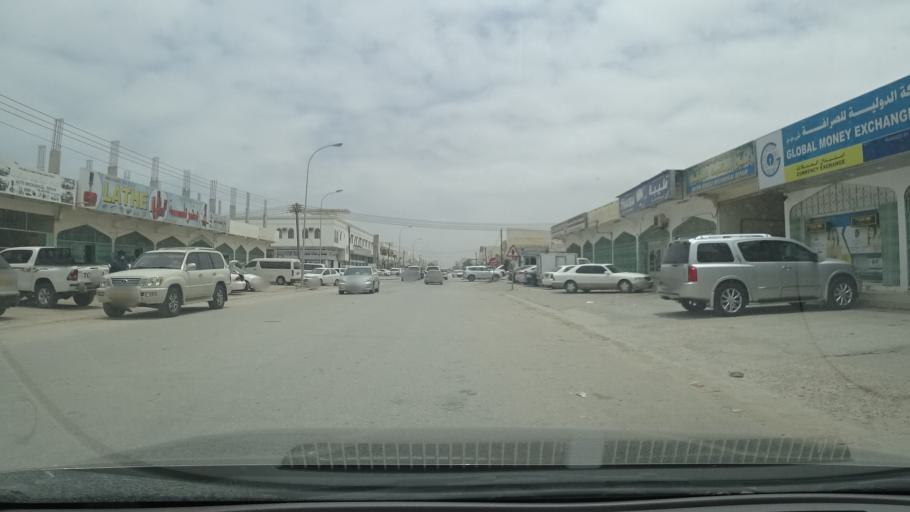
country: OM
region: Zufar
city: Salalah
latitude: 17.0210
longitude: 54.0524
